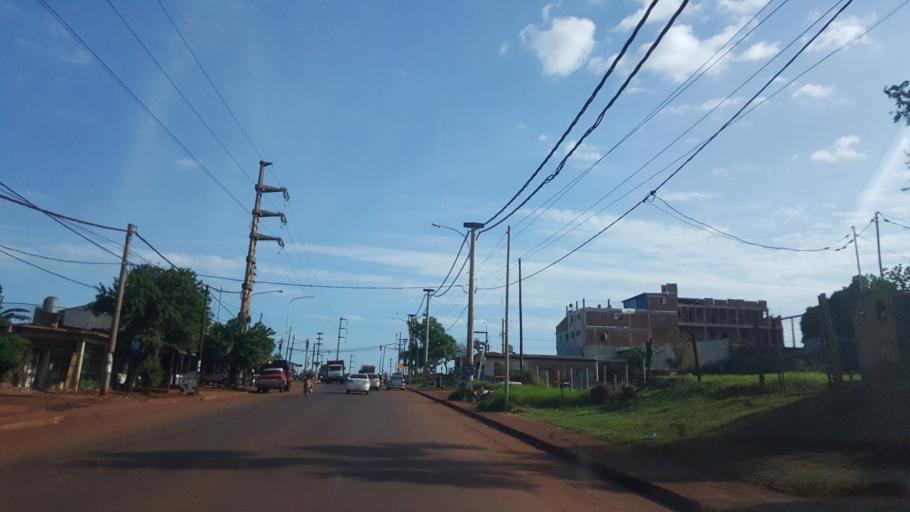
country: AR
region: Misiones
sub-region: Departamento de Capital
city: Posadas
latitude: -27.4265
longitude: -55.9141
